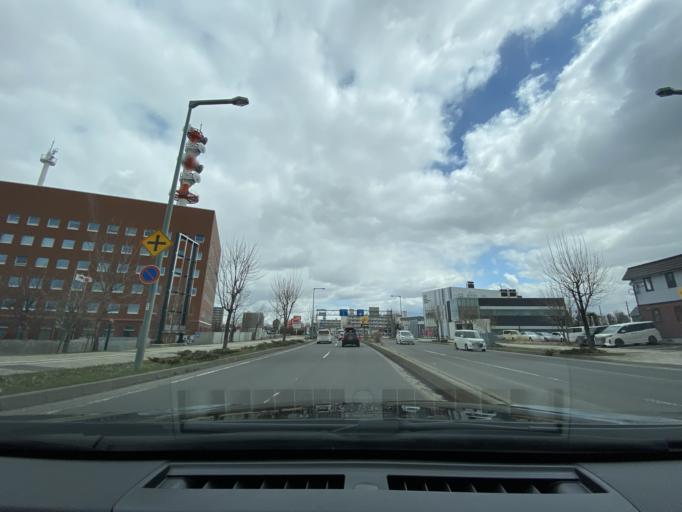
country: JP
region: Hokkaido
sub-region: Asahikawa-shi
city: Asahikawa
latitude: 43.7569
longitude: 142.3730
